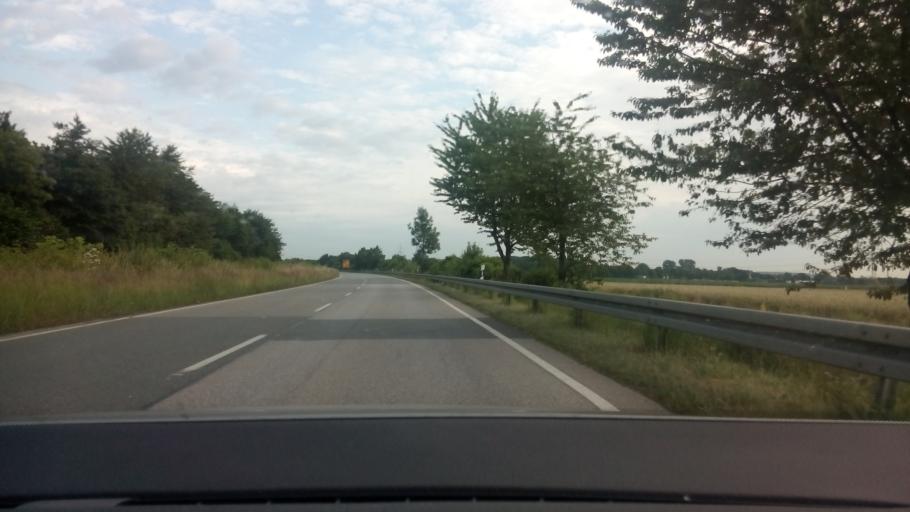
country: DE
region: Bavaria
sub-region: Upper Bavaria
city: Unterschleissheim
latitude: 48.2818
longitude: 11.5906
